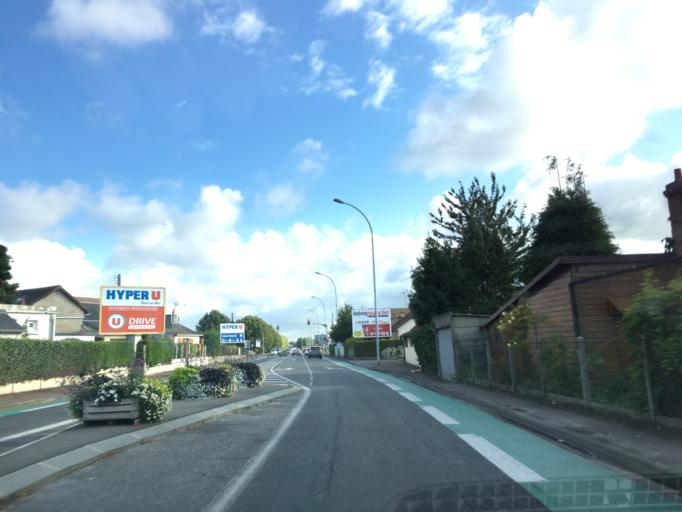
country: FR
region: Lower Normandy
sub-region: Departement du Calvados
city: Dives-sur-Mer
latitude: 49.2847
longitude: -0.1028
